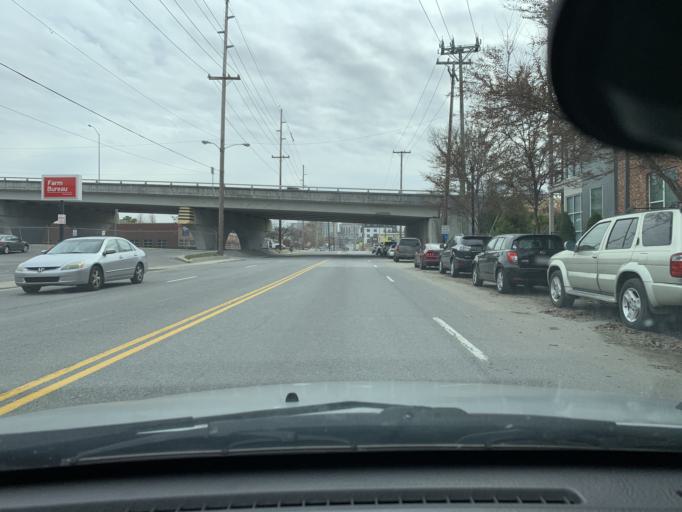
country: US
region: Tennessee
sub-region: Davidson County
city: Nashville
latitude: 36.1758
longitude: -86.7840
